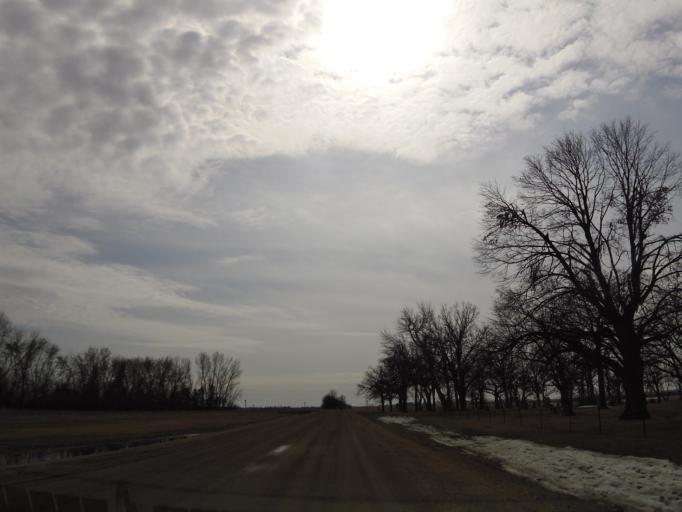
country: US
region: North Dakota
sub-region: Walsh County
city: Grafton
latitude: 48.2830
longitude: -97.3670
